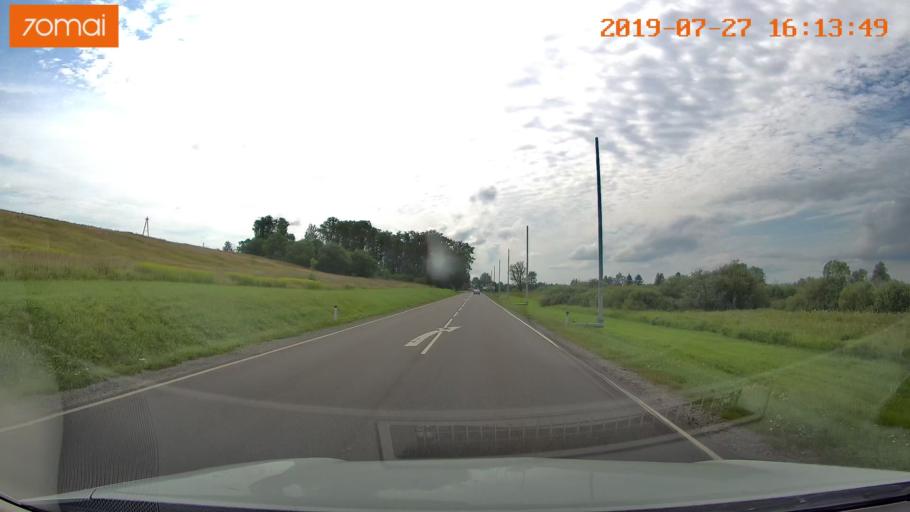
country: RU
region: Kaliningrad
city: Chernyakhovsk
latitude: 54.6281
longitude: 21.6305
